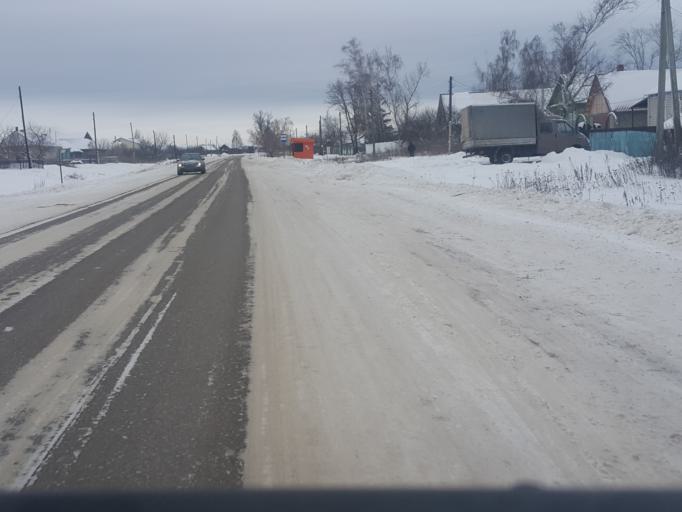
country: RU
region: Tambov
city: Platonovka
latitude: 52.8417
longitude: 41.8122
